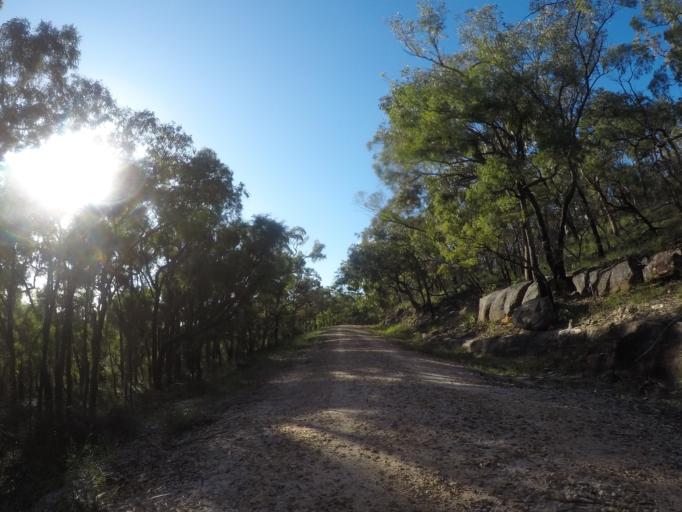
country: AU
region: New South Wales
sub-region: Hornsby Shire
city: Glenorie
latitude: -33.3642
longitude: 150.9898
